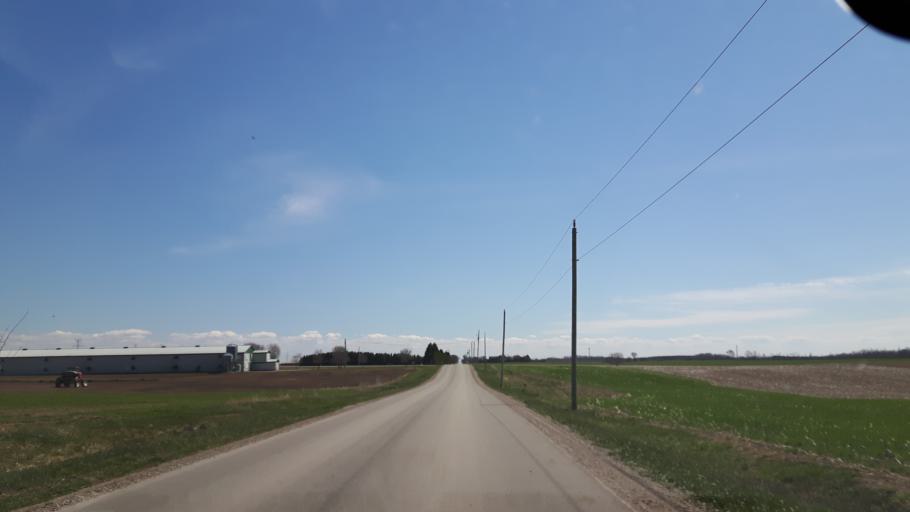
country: CA
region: Ontario
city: Goderich
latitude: 43.6457
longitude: -81.6440
